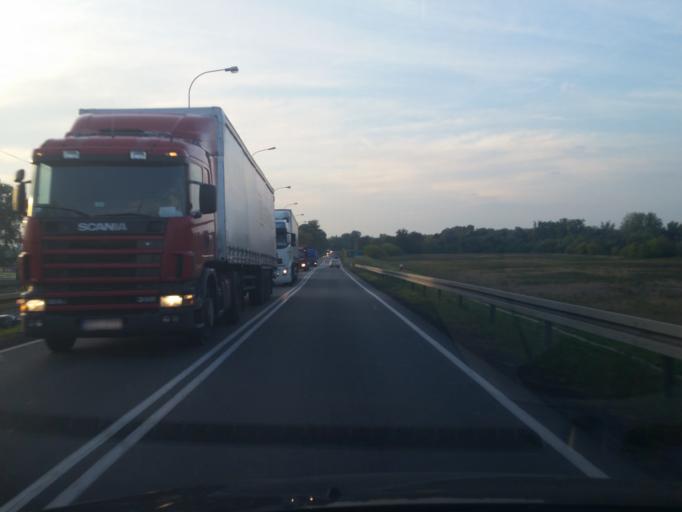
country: PL
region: Masovian Voivodeship
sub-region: Powiat nowodworski
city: Nowy Dwor Mazowiecki
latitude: 52.4117
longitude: 20.6971
